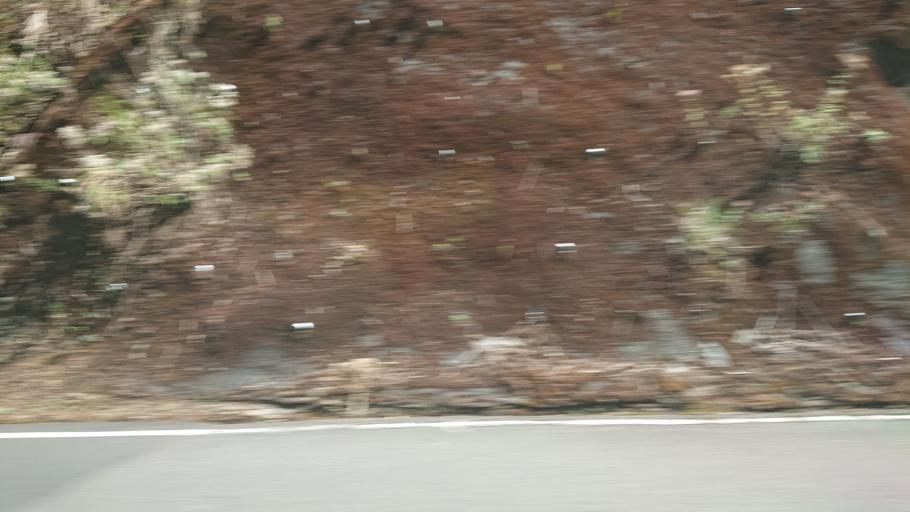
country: TW
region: Taiwan
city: Lugu
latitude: 23.4802
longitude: 120.8526
